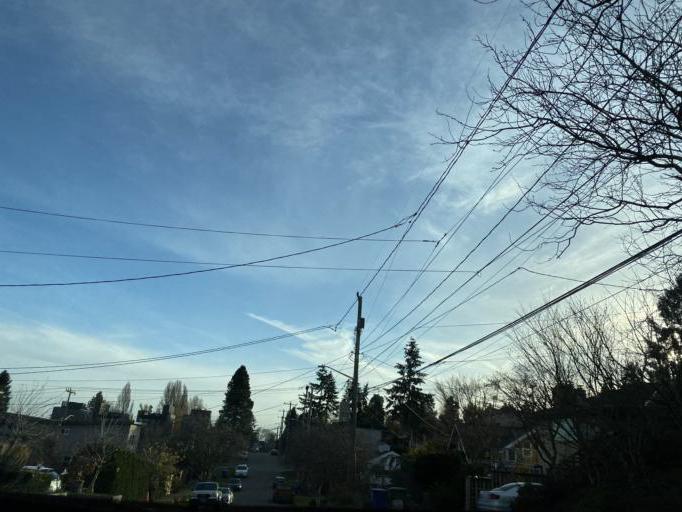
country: US
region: Washington
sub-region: King County
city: Seattle
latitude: 47.6495
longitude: -122.3874
